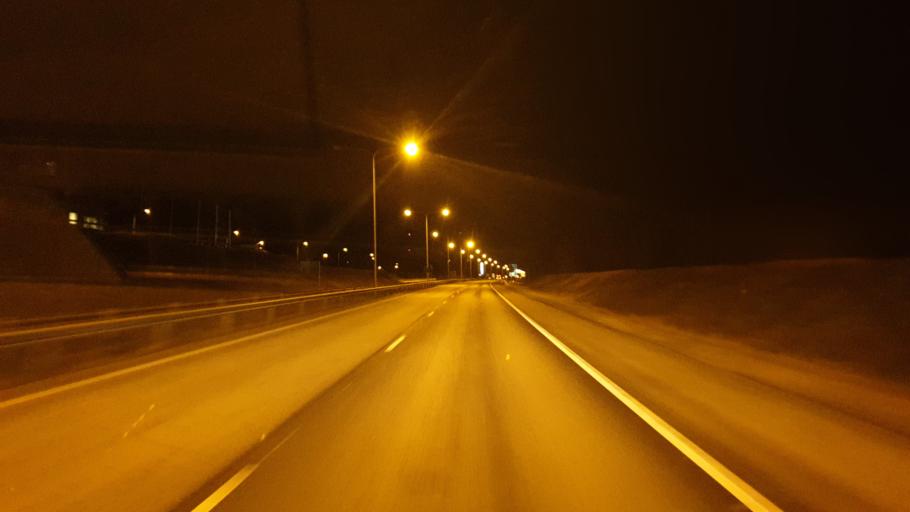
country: FI
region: Central Finland
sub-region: Jyvaeskylae
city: Jyvaeskylae
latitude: 62.2985
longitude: 25.7113
